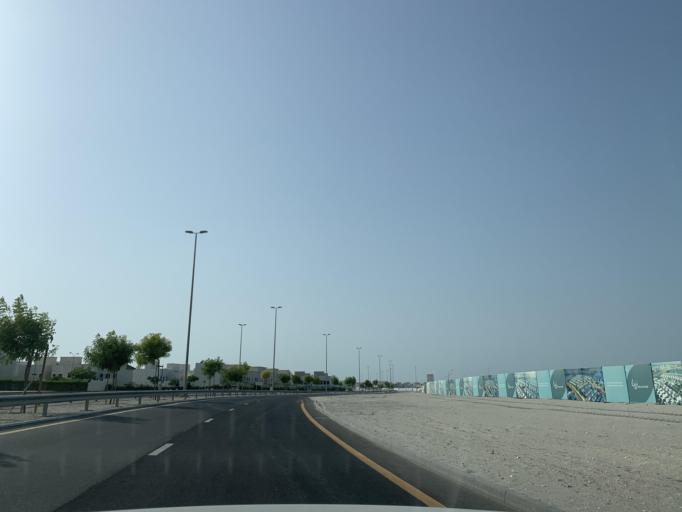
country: BH
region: Muharraq
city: Al Muharraq
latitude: 26.3146
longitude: 50.6323
